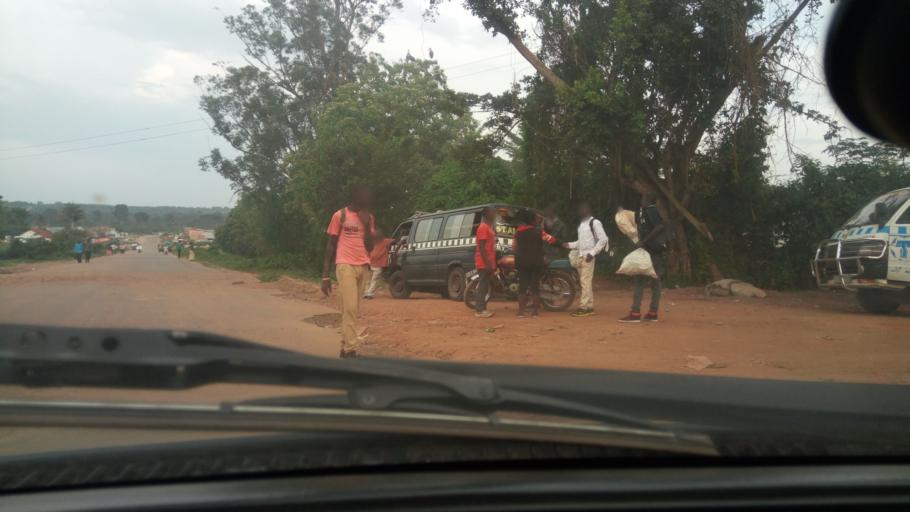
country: UG
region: Central Region
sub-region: Mityana District
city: Mityana
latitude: 0.5653
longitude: 32.2058
